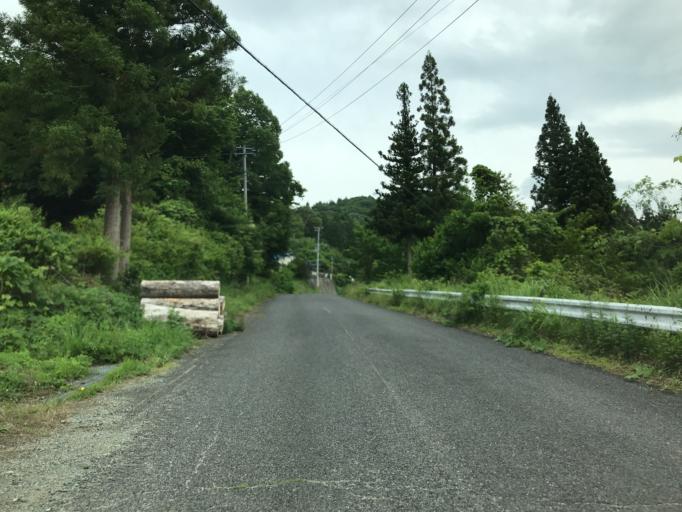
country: JP
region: Fukushima
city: Funehikimachi-funehiki
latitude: 37.4125
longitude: 140.6542
